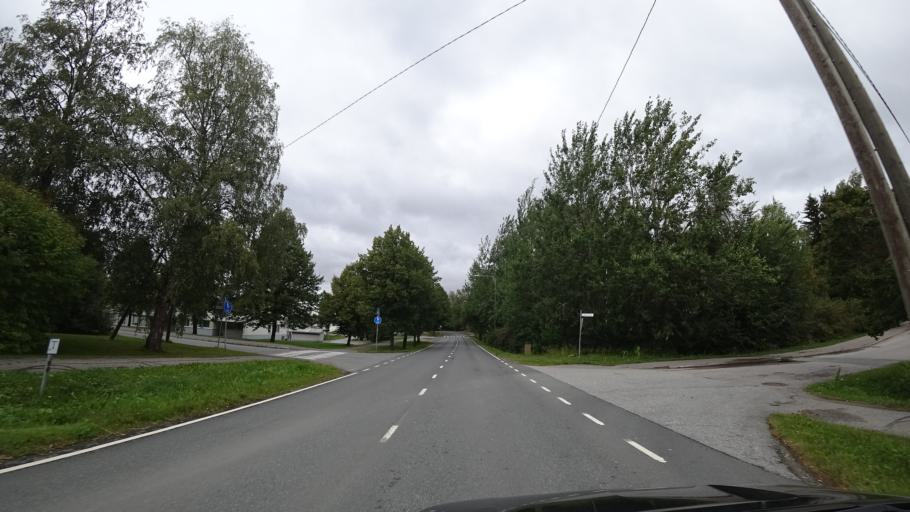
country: FI
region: Haeme
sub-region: Haemeenlinna
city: Lammi
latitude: 61.0821
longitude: 25.0108
